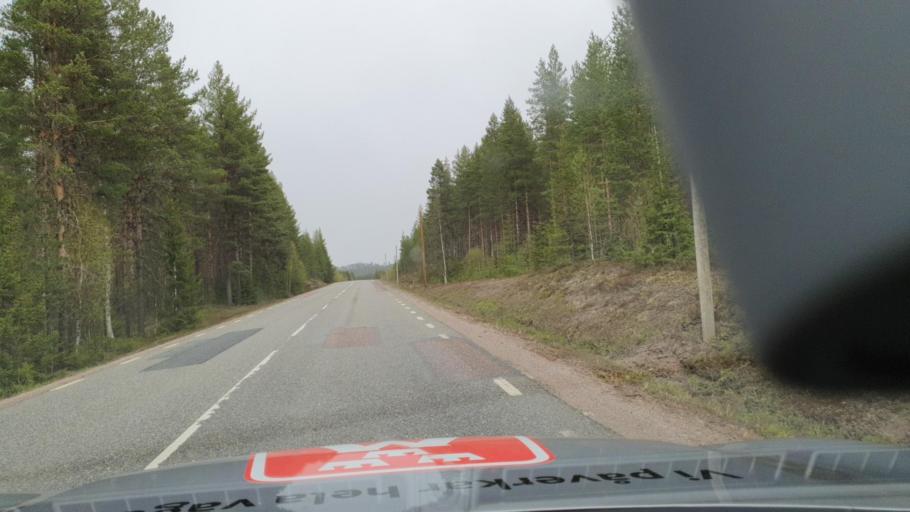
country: SE
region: Vaesterbotten
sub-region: Asele Kommun
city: Asele
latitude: 63.6983
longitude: 17.0391
